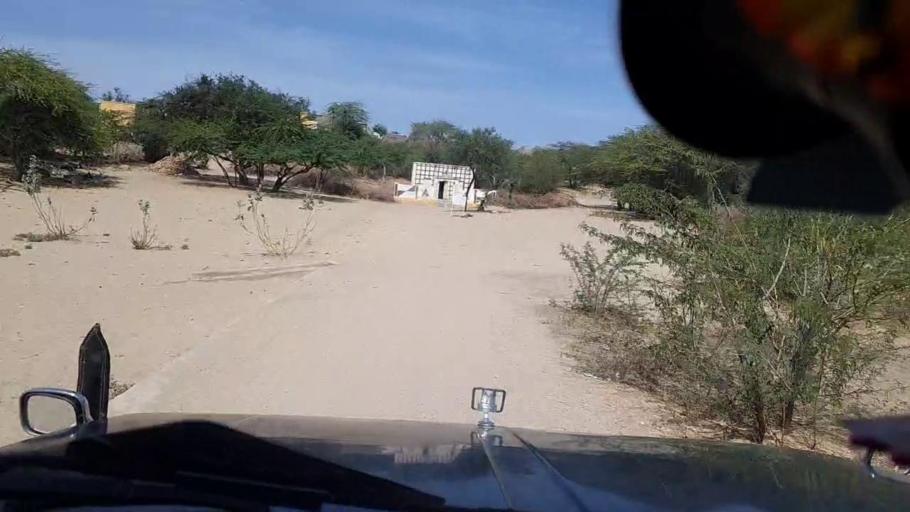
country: PK
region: Sindh
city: Diplo
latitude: 24.4414
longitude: 69.5367
